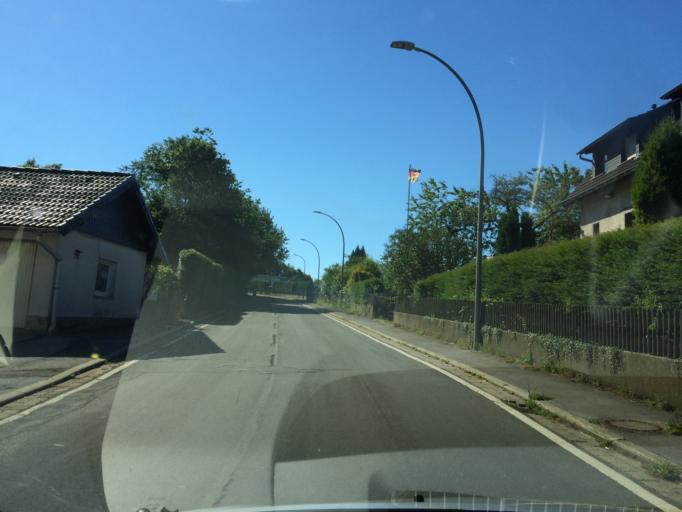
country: DE
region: North Rhine-Westphalia
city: Iserlohn
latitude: 51.3359
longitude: 7.7076
